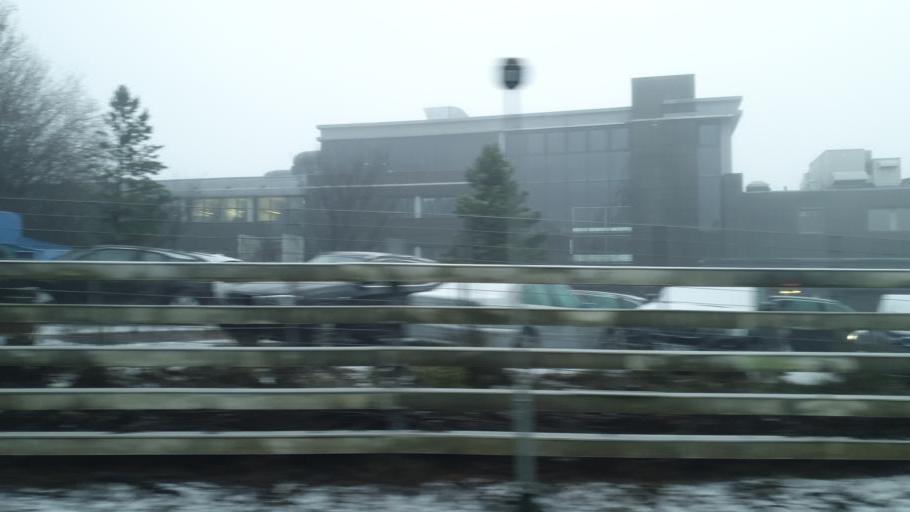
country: NO
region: Oslo
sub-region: Oslo
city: Sjolyststranda
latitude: 59.9188
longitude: 10.6610
